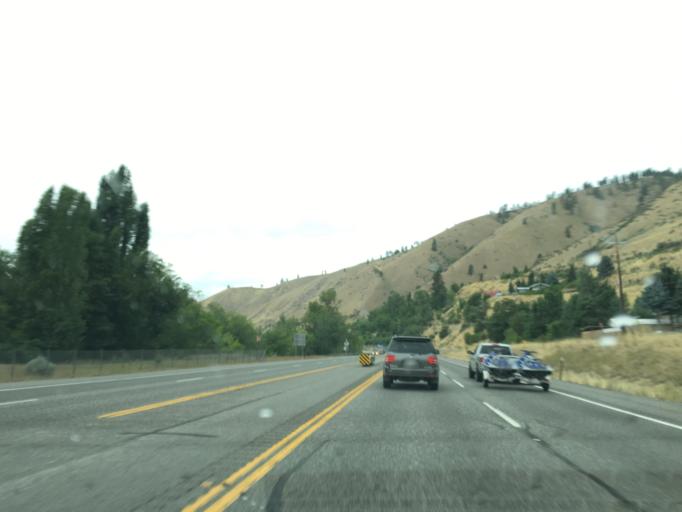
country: US
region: Washington
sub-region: Chelan County
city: Cashmere
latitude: 47.5217
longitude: -120.4556
